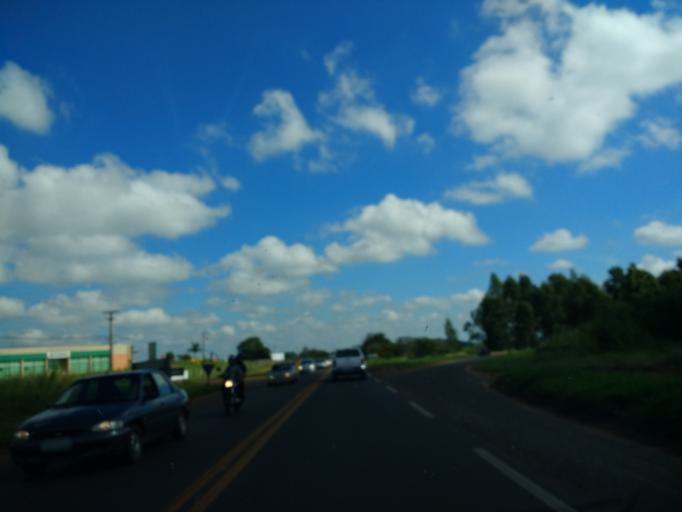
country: BR
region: Parana
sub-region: Umuarama
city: Umuarama
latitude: -23.8123
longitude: -53.3262
